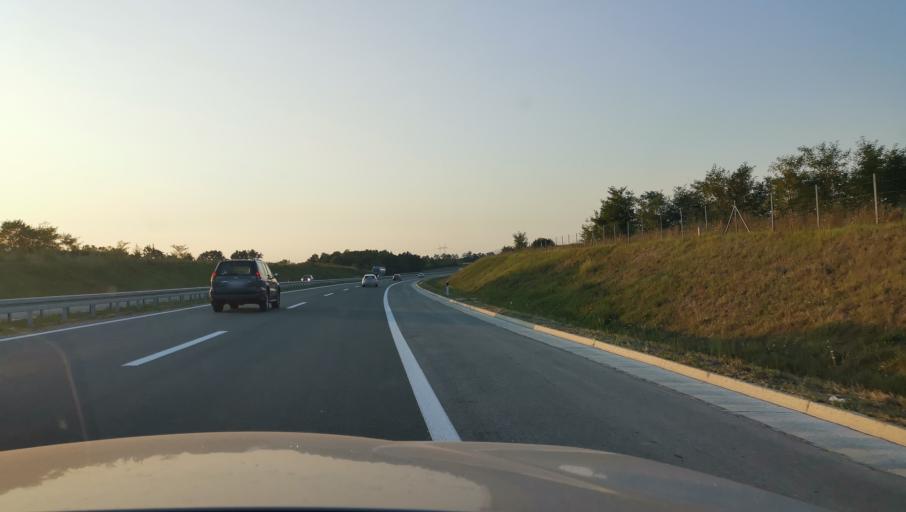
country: RS
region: Central Serbia
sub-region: Kolubarski Okrug
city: Ub
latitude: 44.3962
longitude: 20.0973
